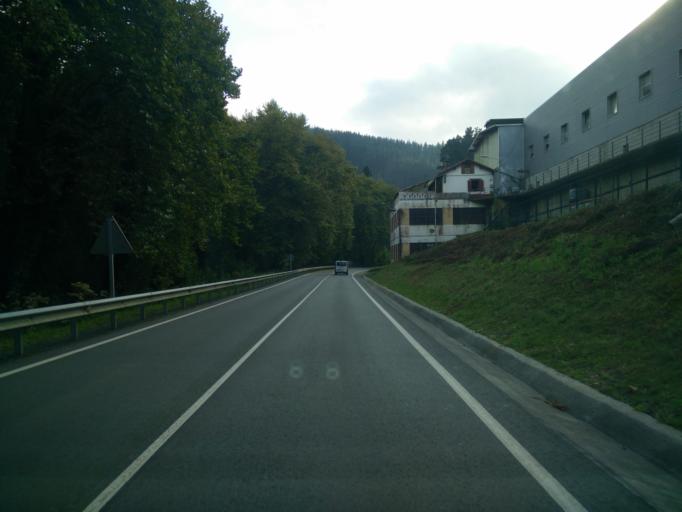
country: ES
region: Basque Country
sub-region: Bizkaia
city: Markina-Xemein
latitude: 43.2892
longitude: -2.4874
